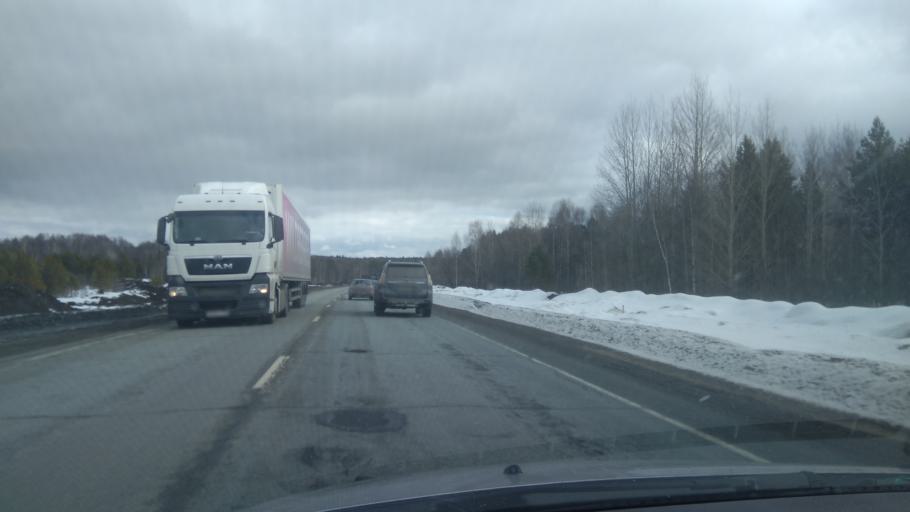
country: RU
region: Sverdlovsk
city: Bisert'
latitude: 56.8350
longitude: 58.9135
